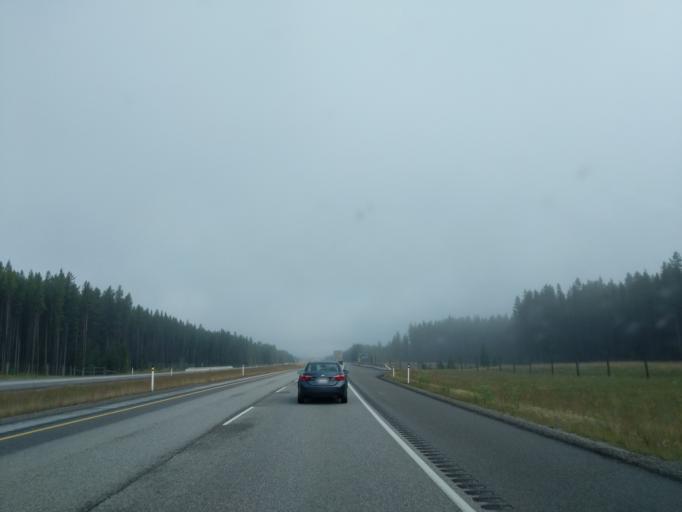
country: CA
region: Alberta
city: Lake Louise
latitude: 51.2903
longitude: -115.9987
